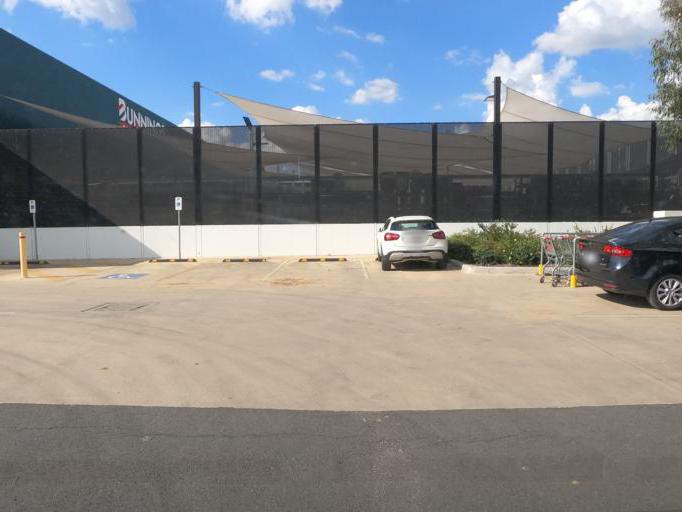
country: AU
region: New South Wales
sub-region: Albury Municipality
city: East Albury
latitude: -36.0747
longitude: 146.9492
